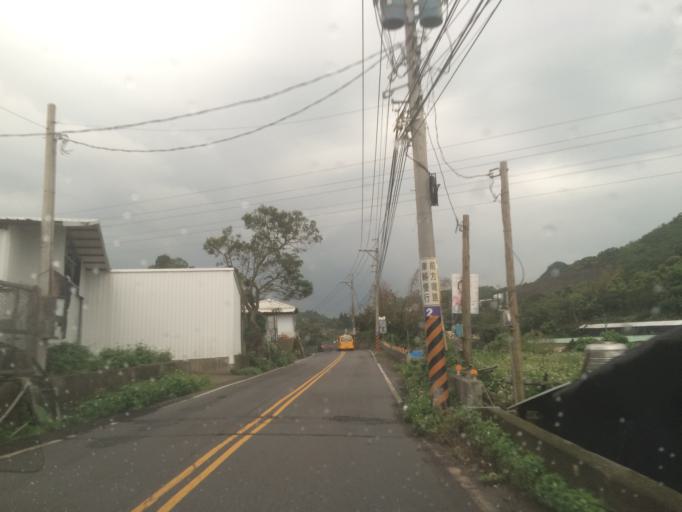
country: TW
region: Taiwan
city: Fengyuan
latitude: 24.1807
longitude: 120.8176
